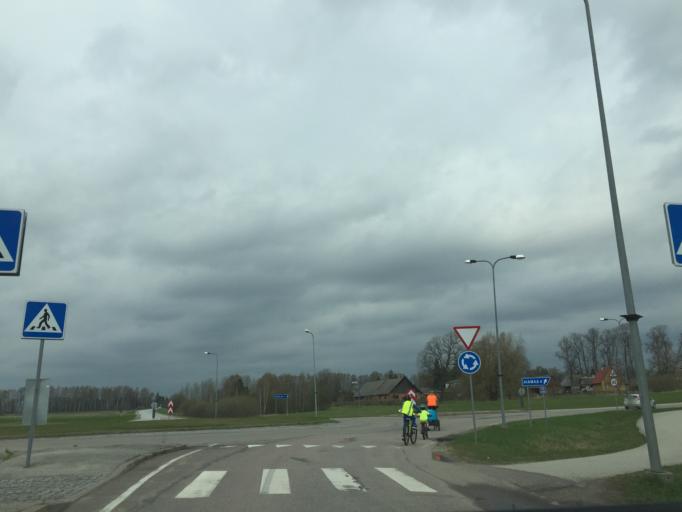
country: EE
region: Tartu
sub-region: Noo vald
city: Noo
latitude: 58.2749
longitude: 26.5322
